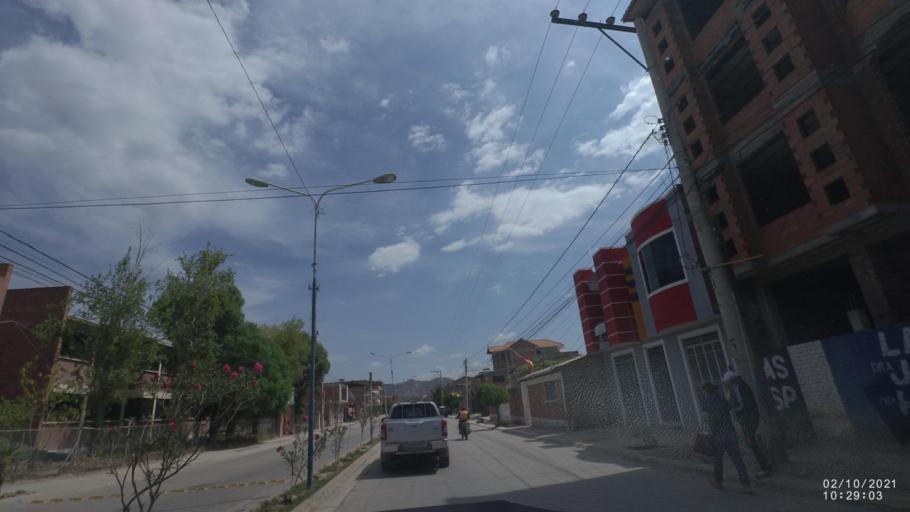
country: BO
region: Cochabamba
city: Capinota
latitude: -17.7081
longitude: -66.2654
